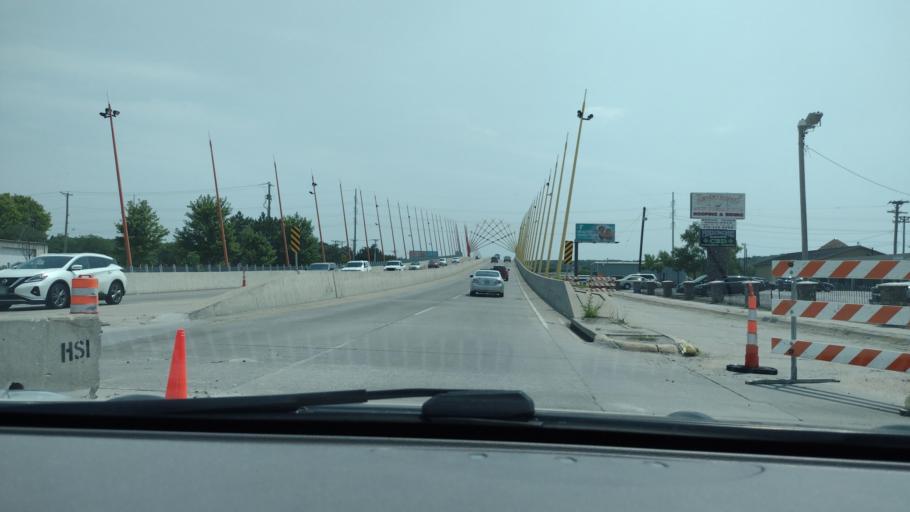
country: US
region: Iowa
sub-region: Pottawattamie County
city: Council Bluffs
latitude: 41.2619
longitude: -95.8659
